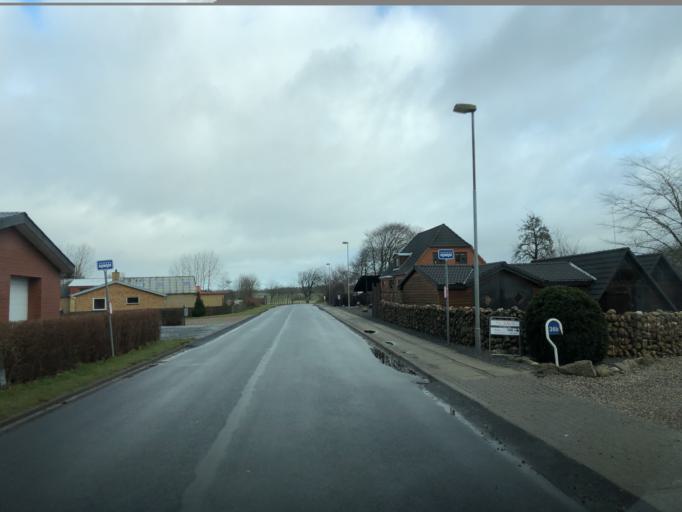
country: DK
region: Central Jutland
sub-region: Skive Kommune
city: Skive
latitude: 56.4474
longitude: 9.0089
